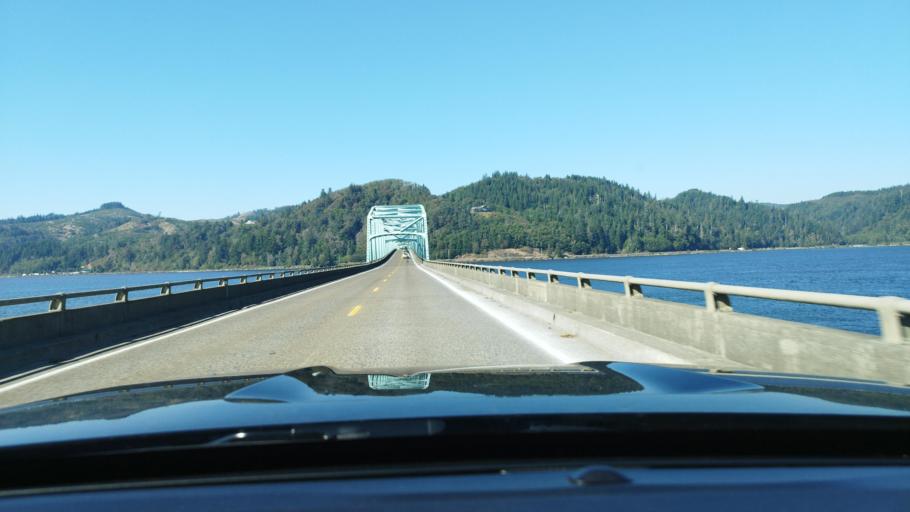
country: US
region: Oregon
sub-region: Clatsop County
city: Astoria
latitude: 46.2330
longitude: -123.8709
